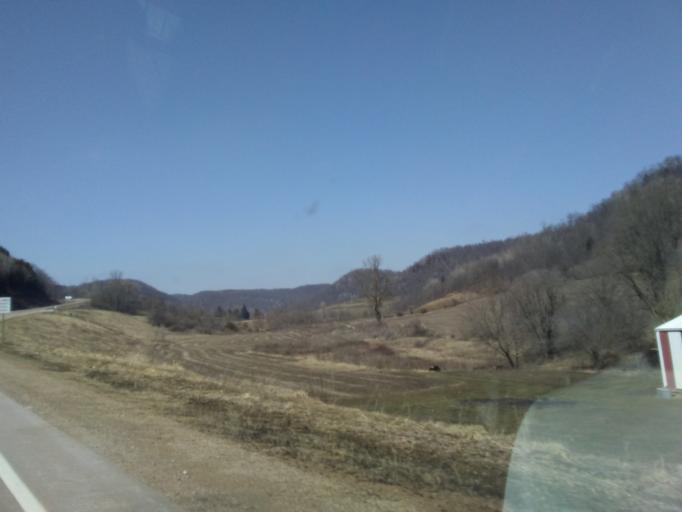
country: US
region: Wisconsin
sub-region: Vernon County
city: Westby
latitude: 43.7025
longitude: -91.0433
